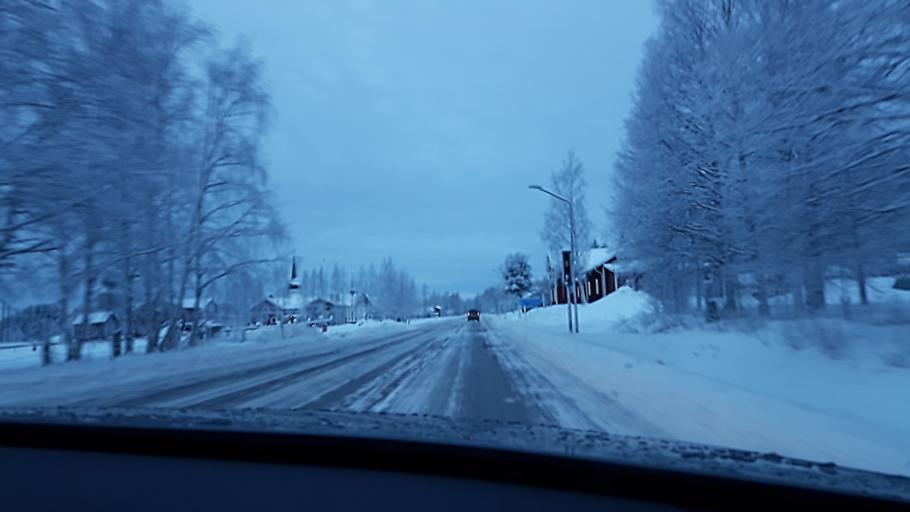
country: SE
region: Jaemtland
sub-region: Harjedalens Kommun
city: Sveg
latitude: 62.0469
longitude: 14.6516
